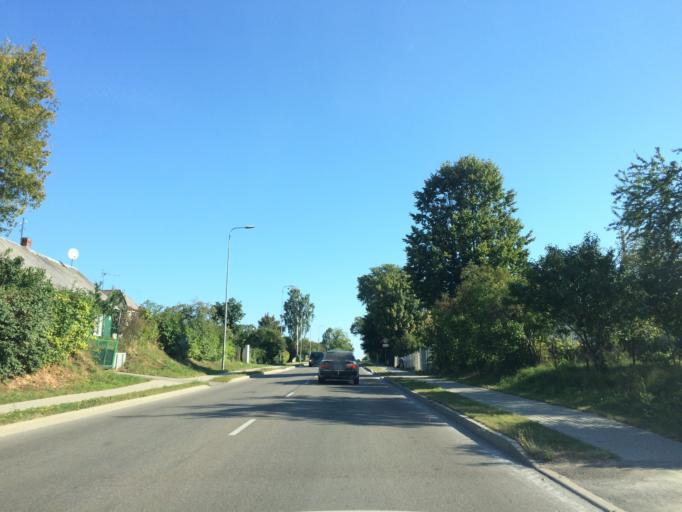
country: LV
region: Rezekne
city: Rezekne
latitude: 56.5068
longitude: 27.3520
